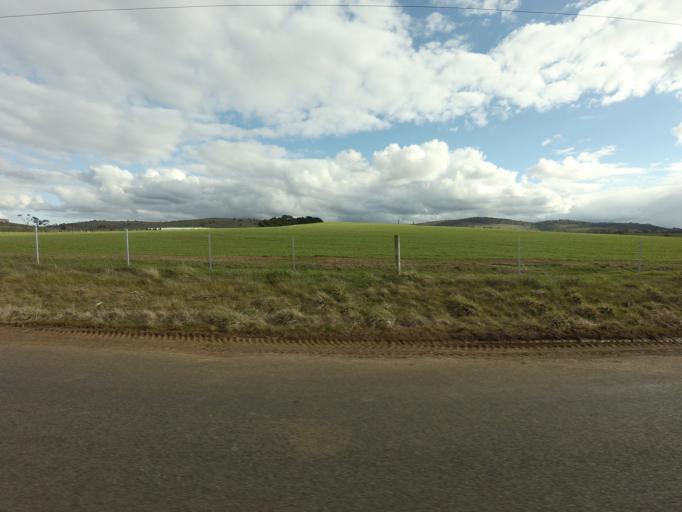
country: AU
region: Tasmania
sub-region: Northern Midlands
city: Evandale
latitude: -41.8936
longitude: 147.3371
